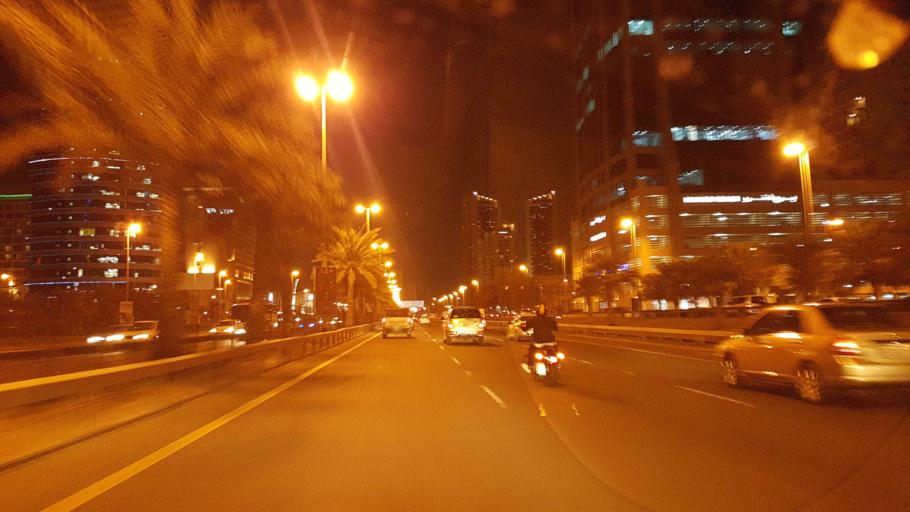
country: BH
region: Manama
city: Jidd Hafs
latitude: 26.2316
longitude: 50.5487
